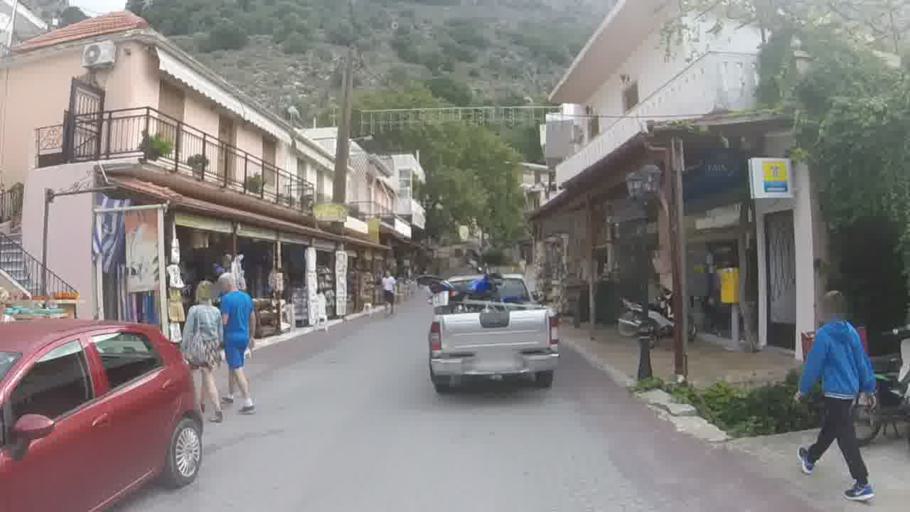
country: GR
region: Crete
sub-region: Nomos Rethymnis
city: Agia Foteini
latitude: 35.2180
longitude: 24.5355
